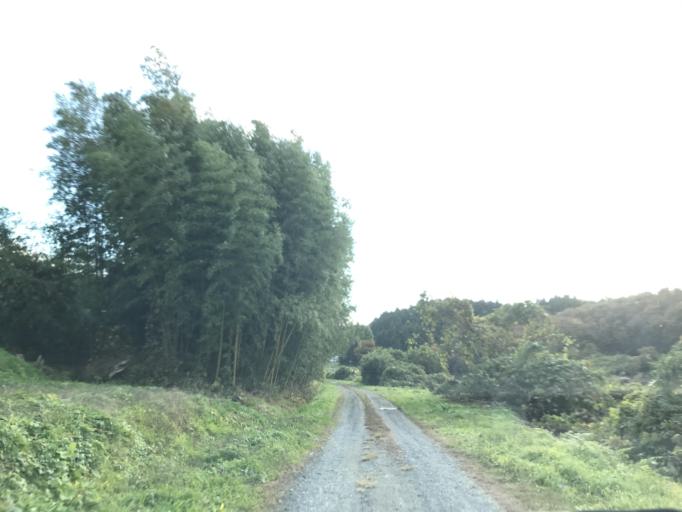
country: JP
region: Iwate
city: Ichinoseki
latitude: 38.8707
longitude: 141.1380
